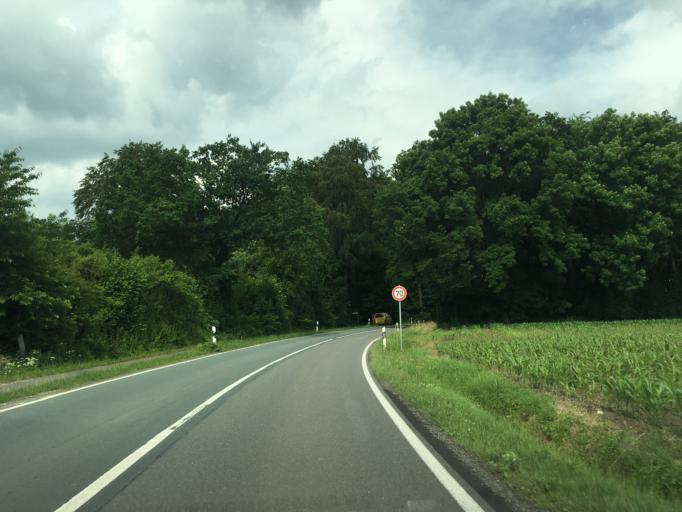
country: DE
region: North Rhine-Westphalia
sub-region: Regierungsbezirk Munster
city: Havixbeck
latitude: 51.9817
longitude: 7.3985
